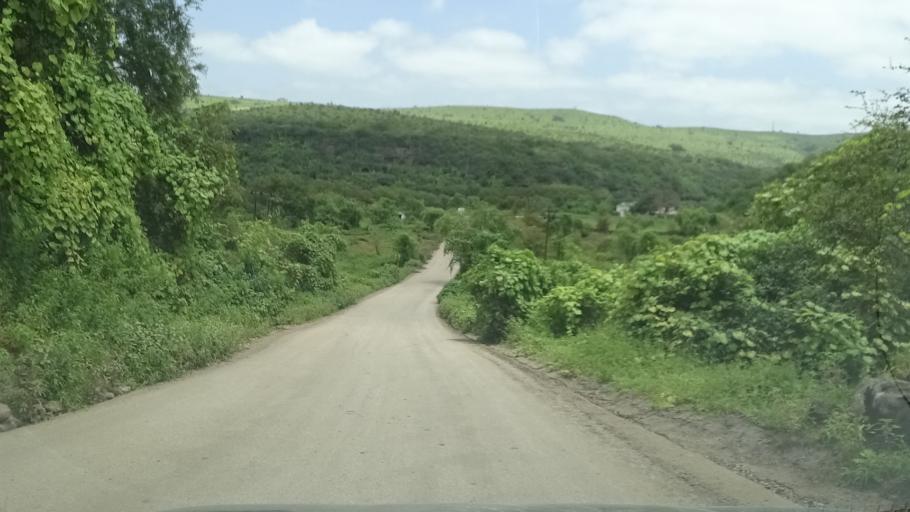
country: OM
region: Zufar
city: Salalah
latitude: 17.1962
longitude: 54.1798
